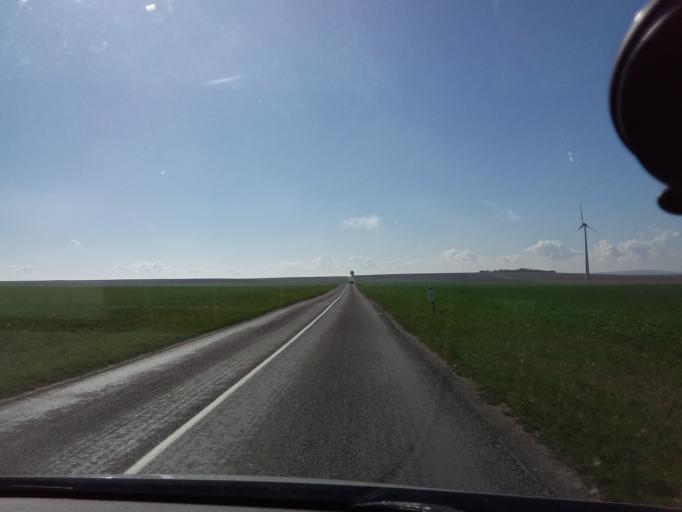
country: FR
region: Picardie
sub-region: Departement de l'Aisne
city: Guignicourt
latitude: 49.5204
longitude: 4.0430
